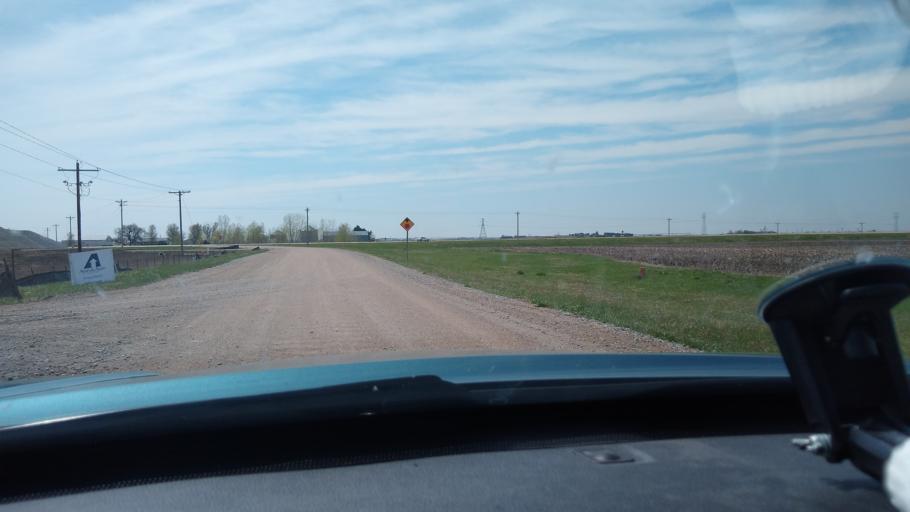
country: US
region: Nebraska
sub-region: Fillmore County
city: Geneva
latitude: 40.4155
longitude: -97.5916
